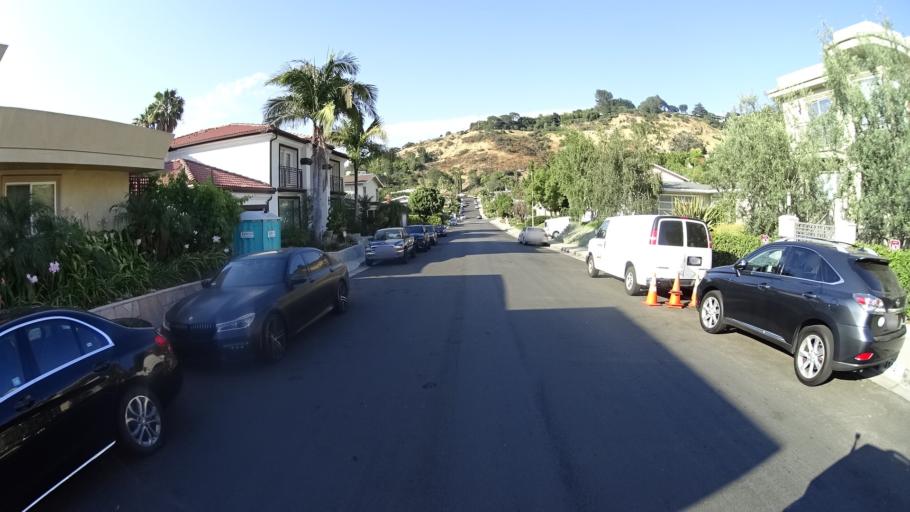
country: US
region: California
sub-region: Los Angeles County
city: Universal City
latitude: 34.1280
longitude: -118.3762
